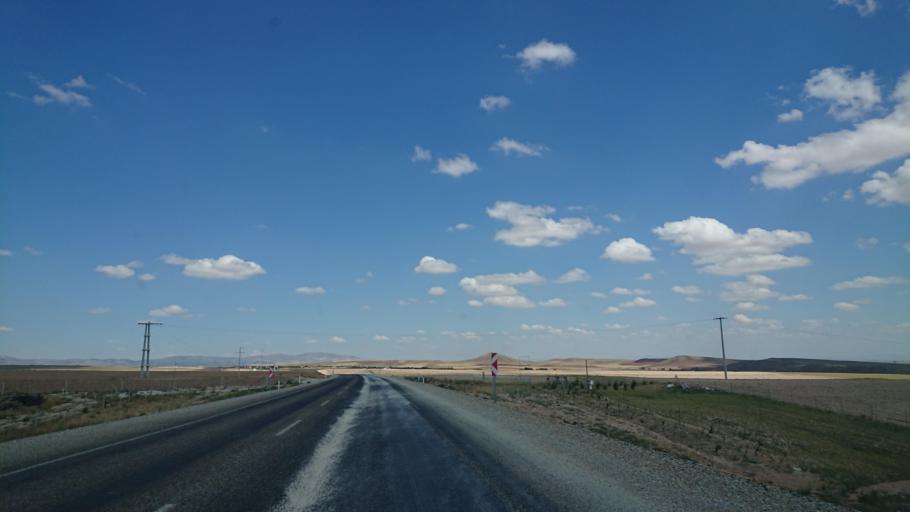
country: TR
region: Kirsehir
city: Kirsehir
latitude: 39.1221
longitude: 34.0068
